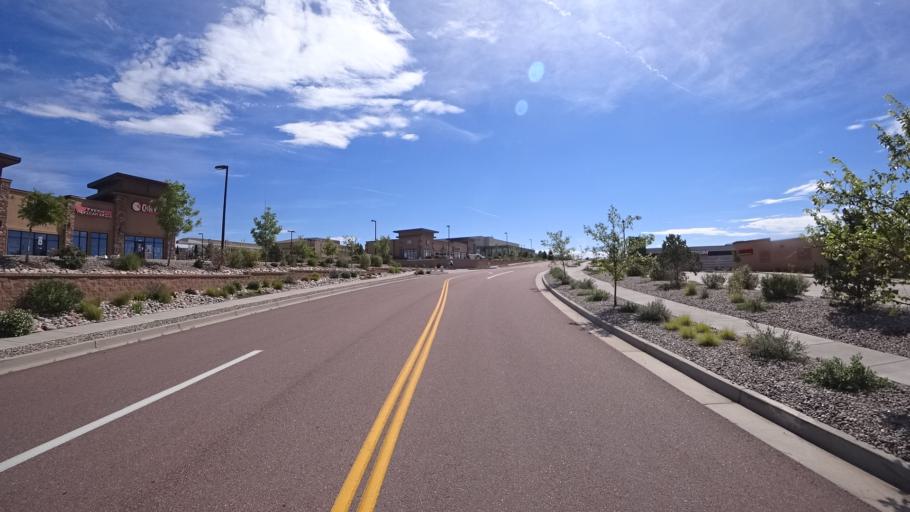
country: US
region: Colorado
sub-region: El Paso County
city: Gleneagle
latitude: 39.0258
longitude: -104.8239
